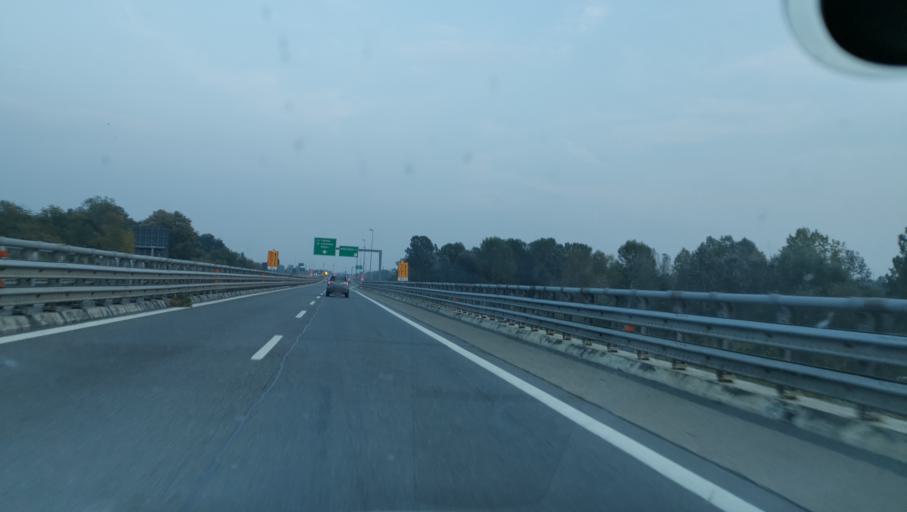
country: IT
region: Piedmont
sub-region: Provincia di Torino
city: Drubiaglio-Grangia
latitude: 45.0923
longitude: 7.4106
